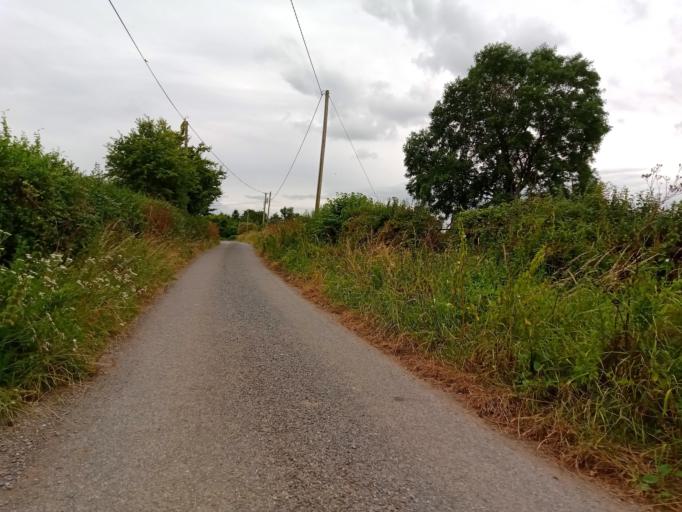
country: IE
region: Leinster
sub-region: Kilkenny
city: Callan
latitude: 52.5404
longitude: -7.4155
